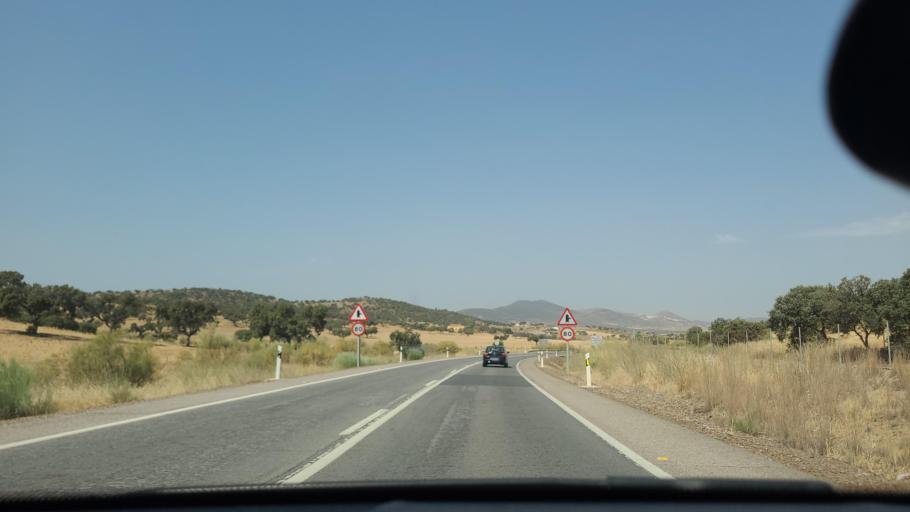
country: ES
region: Extremadura
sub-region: Provincia de Badajoz
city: Fuente del Maestre
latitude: 38.4737
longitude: -6.4569
